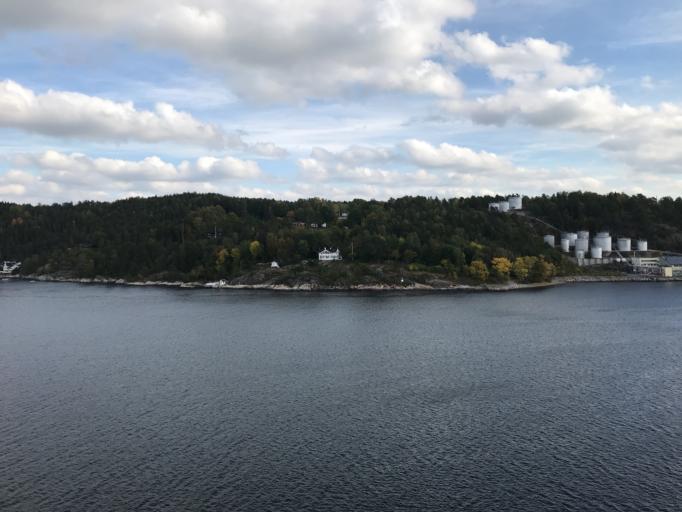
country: NO
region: Akershus
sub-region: Nesodden
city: Fagerstrand
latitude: 59.7403
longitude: 10.5757
